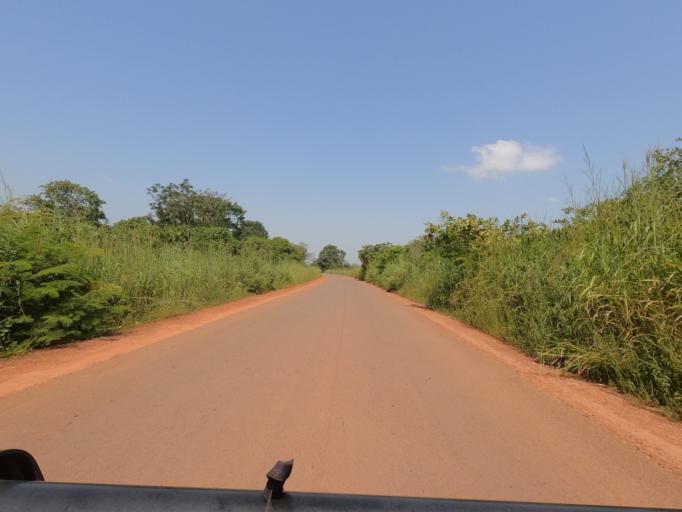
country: SN
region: Ziguinchor
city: Adeane
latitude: 12.3879
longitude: -15.7821
